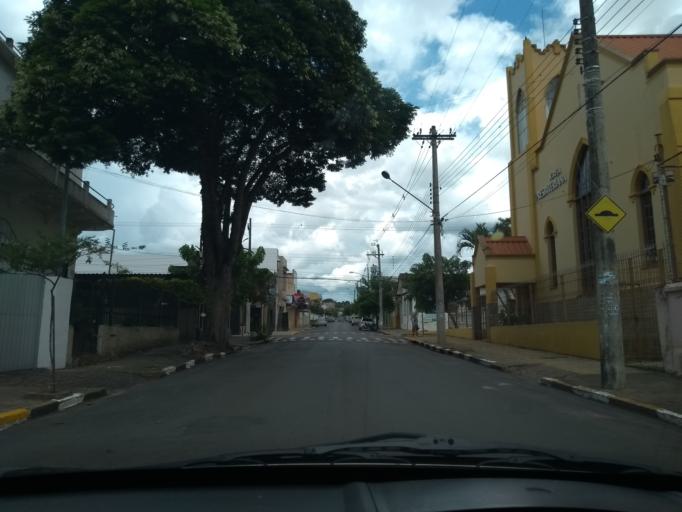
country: BR
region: Sao Paulo
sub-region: Casa Branca
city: Casa Branca
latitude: -21.7755
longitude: -47.0833
